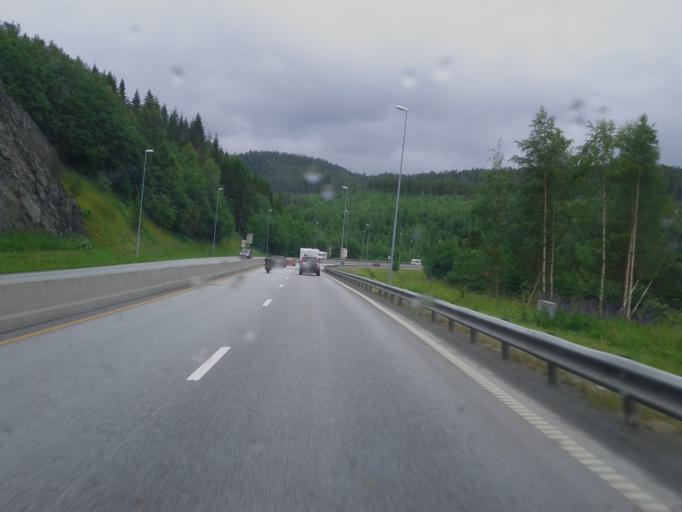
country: NO
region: Sor-Trondelag
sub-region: Malvik
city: Hommelvik
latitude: 63.4087
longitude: 10.8160
